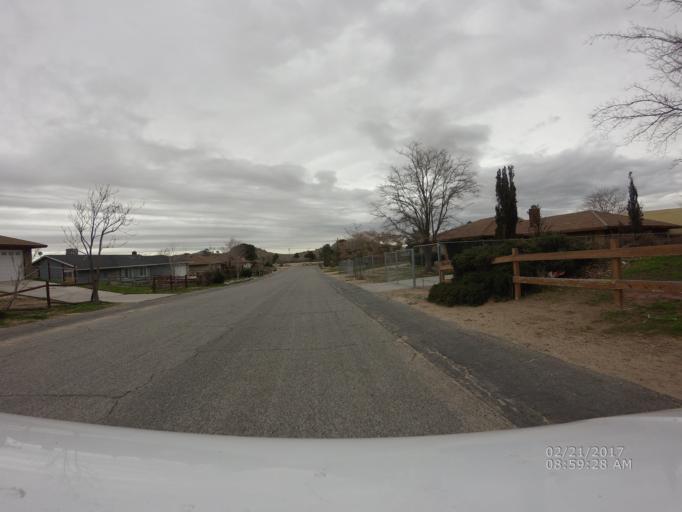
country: US
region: California
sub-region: Los Angeles County
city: Lake Los Angeles
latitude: 34.6019
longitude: -117.8313
